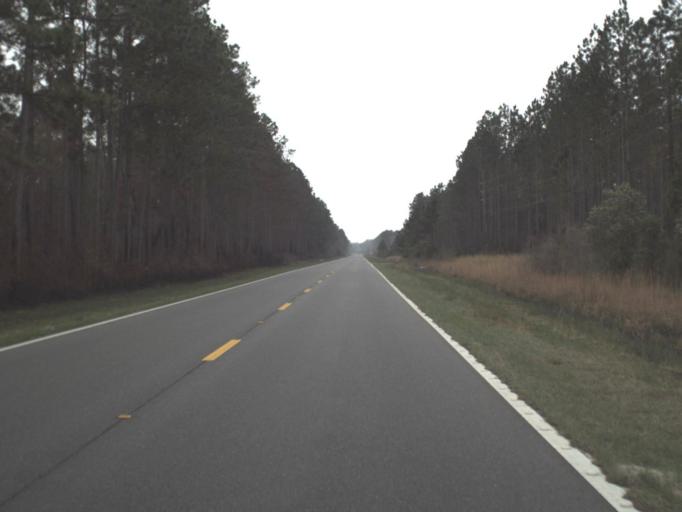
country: US
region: Florida
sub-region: Liberty County
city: Bristol
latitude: 30.2892
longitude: -84.8369
